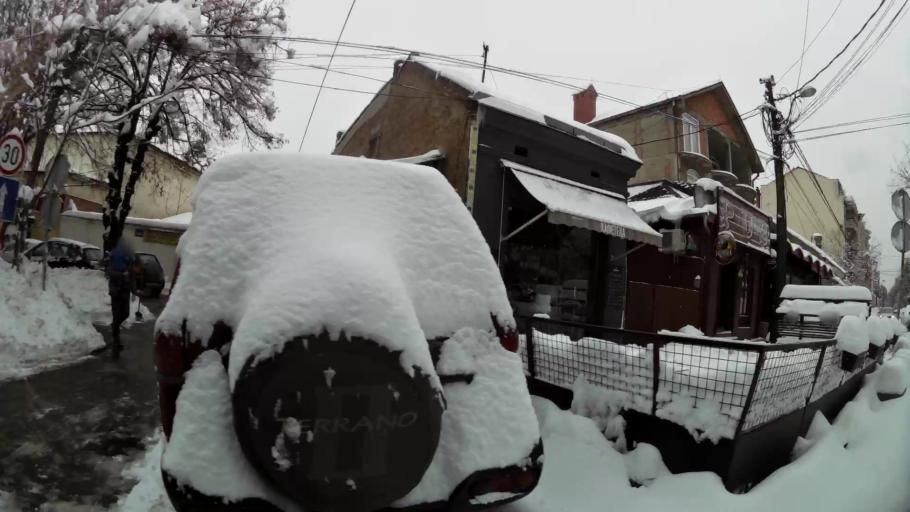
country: RS
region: Central Serbia
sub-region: Belgrade
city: Vracar
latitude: 44.7993
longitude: 20.4853
